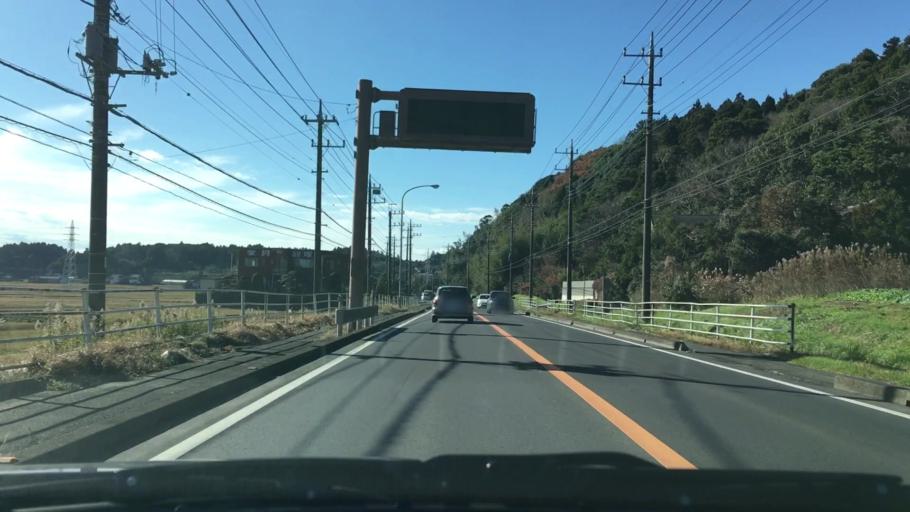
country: JP
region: Chiba
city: Omigawa
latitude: 35.8459
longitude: 140.5758
